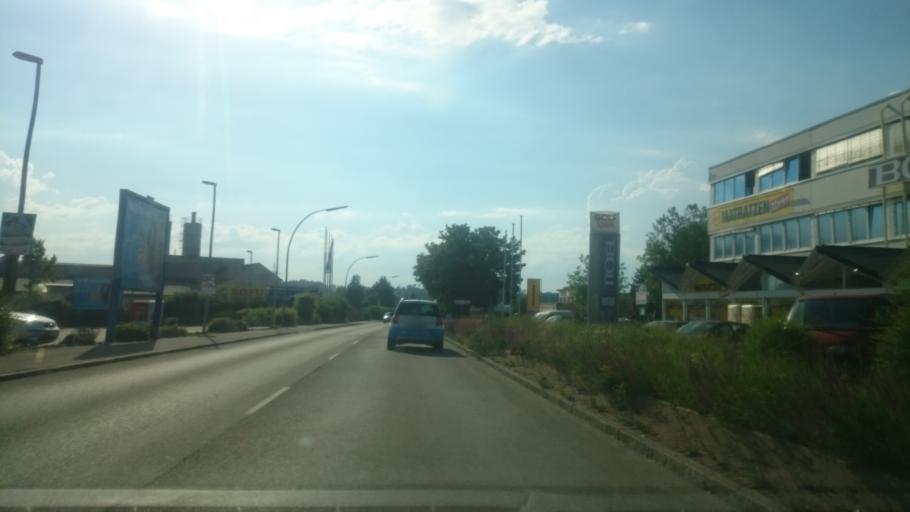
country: DE
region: Baden-Wuerttemberg
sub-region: Tuebingen Region
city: Mossingen
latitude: 48.4072
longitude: 9.0451
